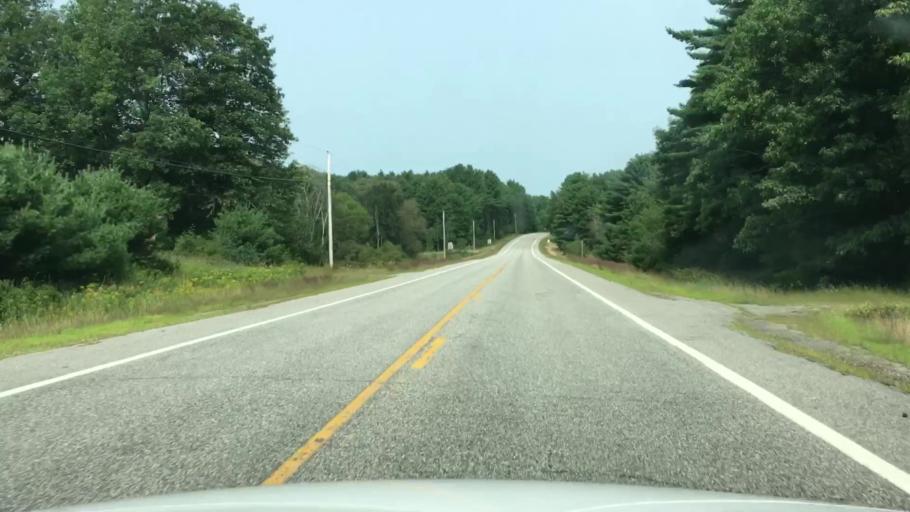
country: US
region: Maine
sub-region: Kennebec County
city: Wayne
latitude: 44.3584
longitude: -70.0826
